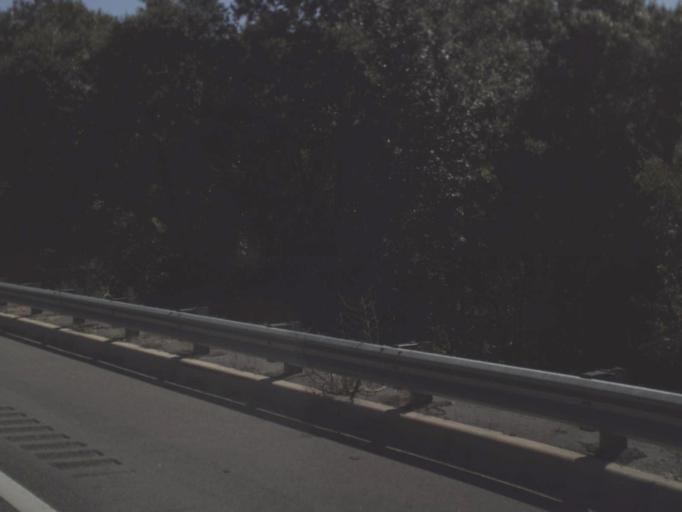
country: US
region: Florida
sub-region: Orange County
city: Oakland
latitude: 28.5559
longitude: -81.6695
